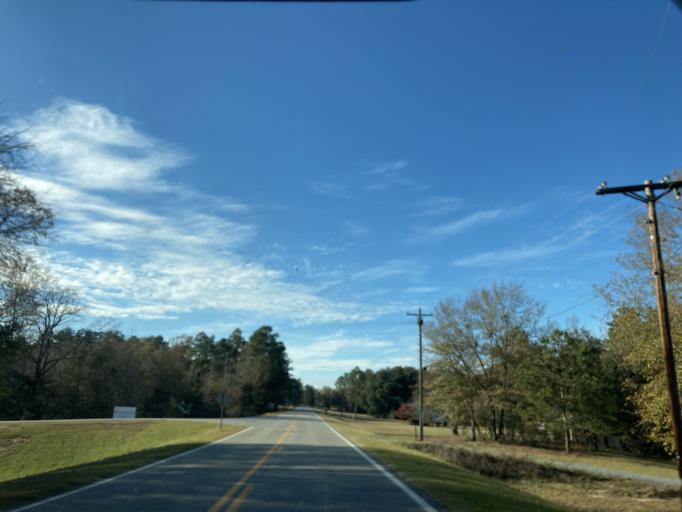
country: US
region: Georgia
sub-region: Jones County
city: Gray
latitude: 32.8963
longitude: -83.5137
